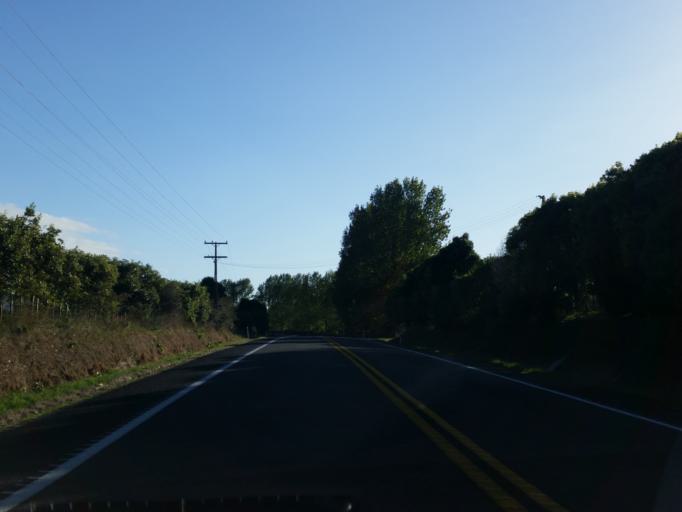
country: NZ
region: Bay of Plenty
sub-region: Western Bay of Plenty District
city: Waihi Beach
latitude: -37.4482
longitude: 175.8785
